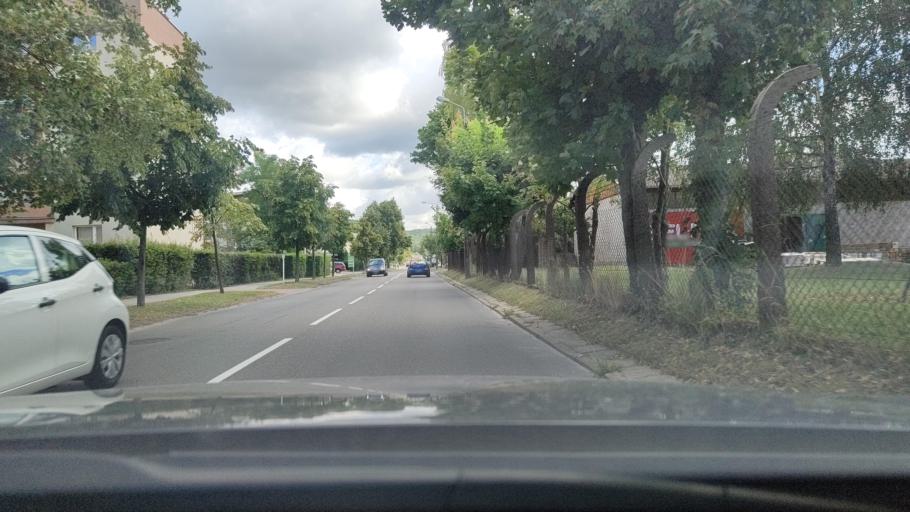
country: PL
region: Pomeranian Voivodeship
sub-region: Powiat wejherowski
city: Wejherowo
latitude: 54.6089
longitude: 18.2241
